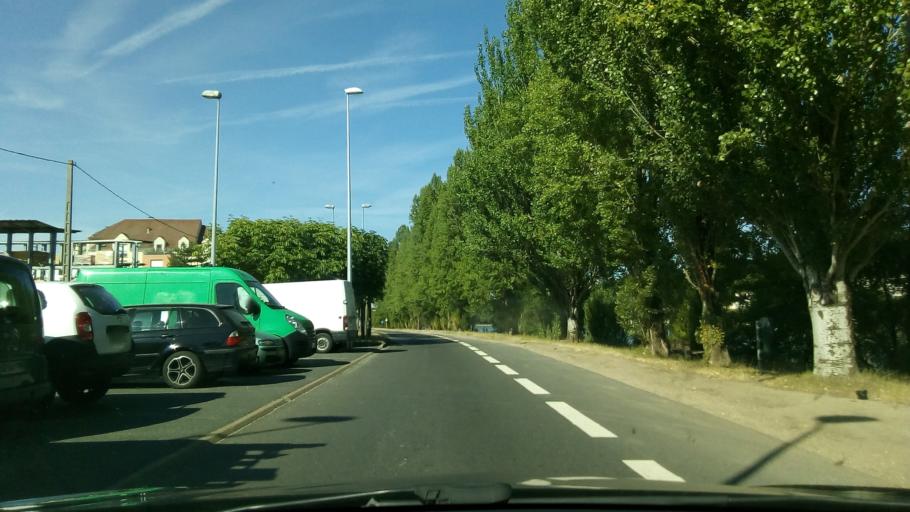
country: FR
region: Ile-de-France
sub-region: Departement de Seine-et-Marne
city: Melun
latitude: 48.5357
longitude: 2.6483
